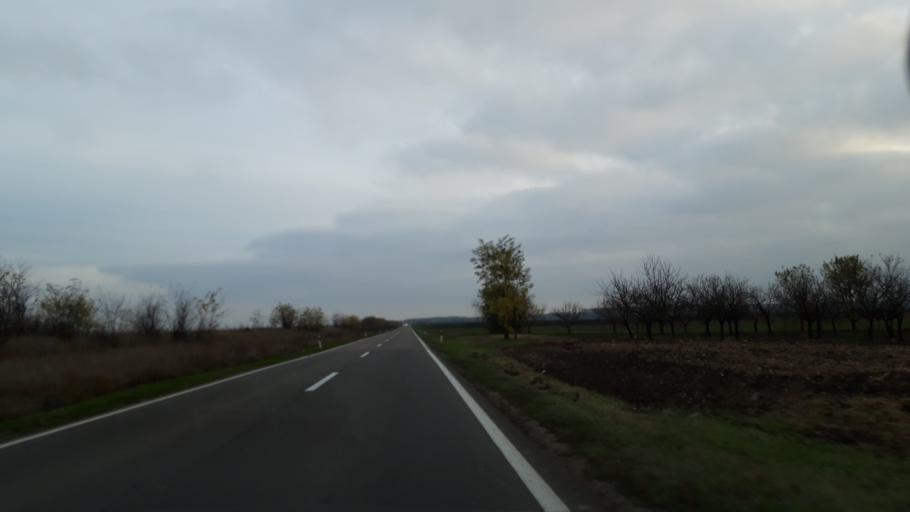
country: RS
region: Autonomna Pokrajina Vojvodina
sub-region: Severnobanatski Okrug
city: Novi Knezevac
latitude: 46.0127
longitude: 20.0983
